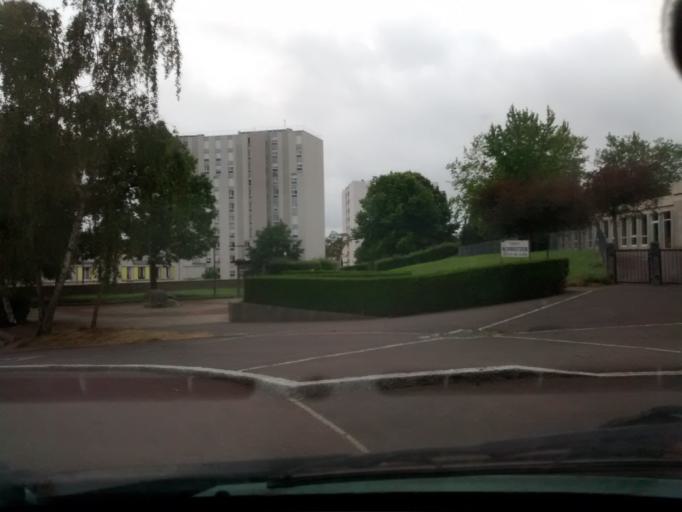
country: FR
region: Lower Normandy
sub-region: Departement de la Manche
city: Saint-Lo
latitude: 49.1139
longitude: -1.0720
